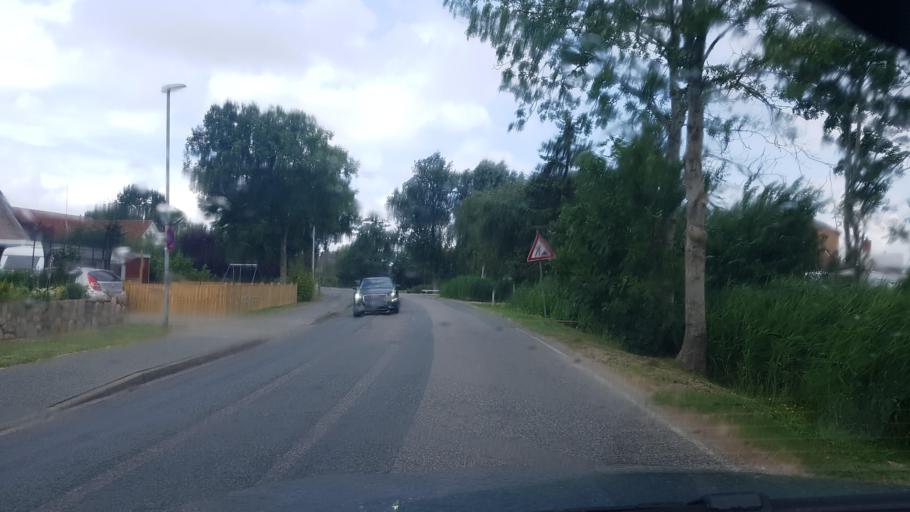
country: DE
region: Schleswig-Holstein
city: Elisabeth-Sophien-Koog
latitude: 54.4923
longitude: 8.8653
